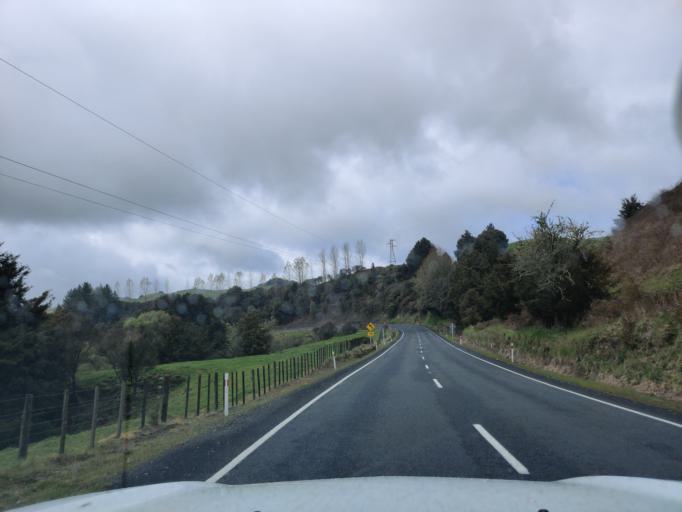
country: NZ
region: Waikato
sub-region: Otorohanga District
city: Otorohanga
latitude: -38.6952
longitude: 175.2200
